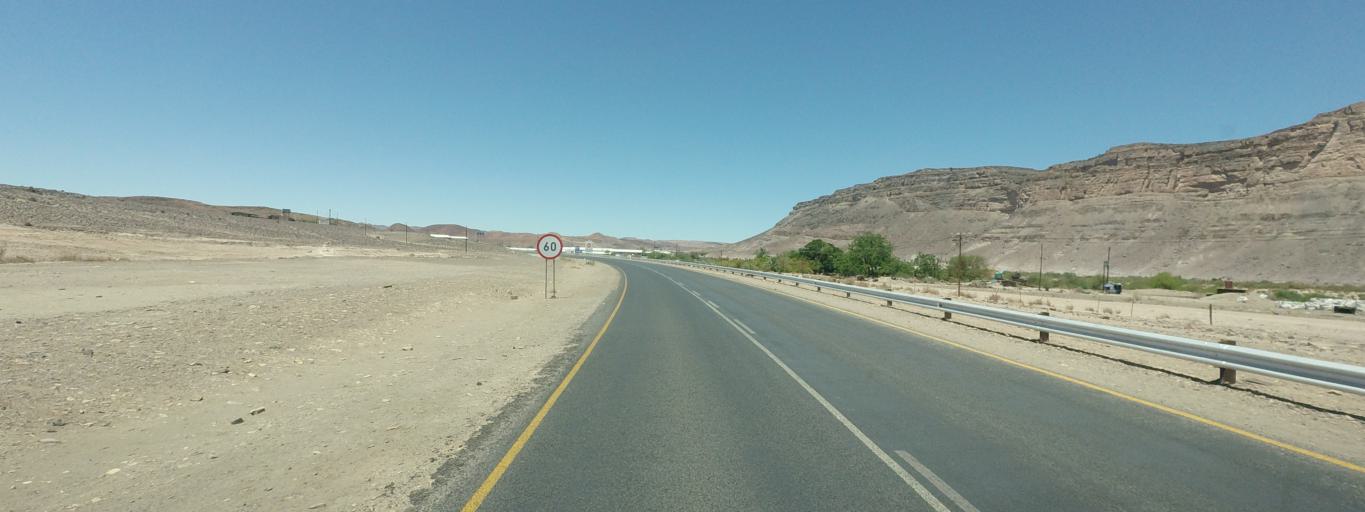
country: ZA
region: Northern Cape
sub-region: Namakwa District Municipality
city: Port Nolloth
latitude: -28.7532
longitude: 17.6195
